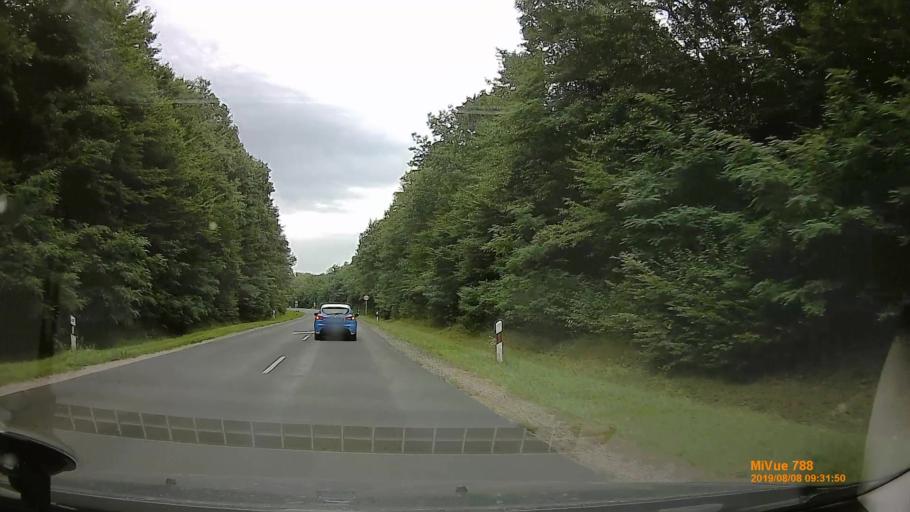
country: HU
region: Vas
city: Vasvar
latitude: 47.0033
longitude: 16.8285
